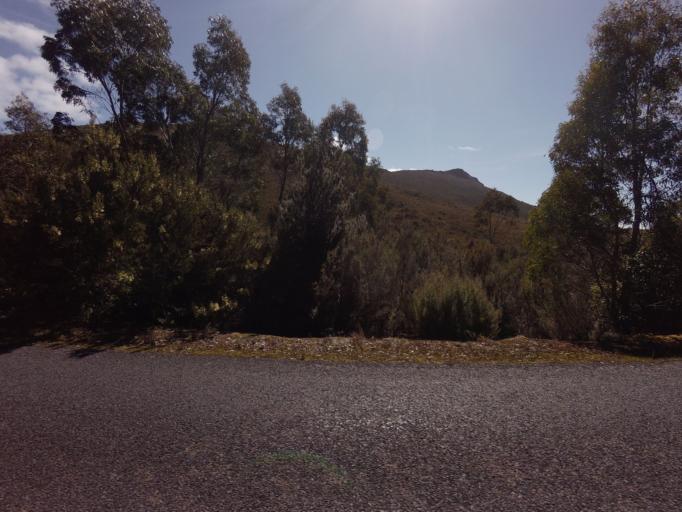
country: AU
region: Tasmania
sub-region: Derwent Valley
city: New Norfolk
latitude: -42.7241
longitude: 146.4478
